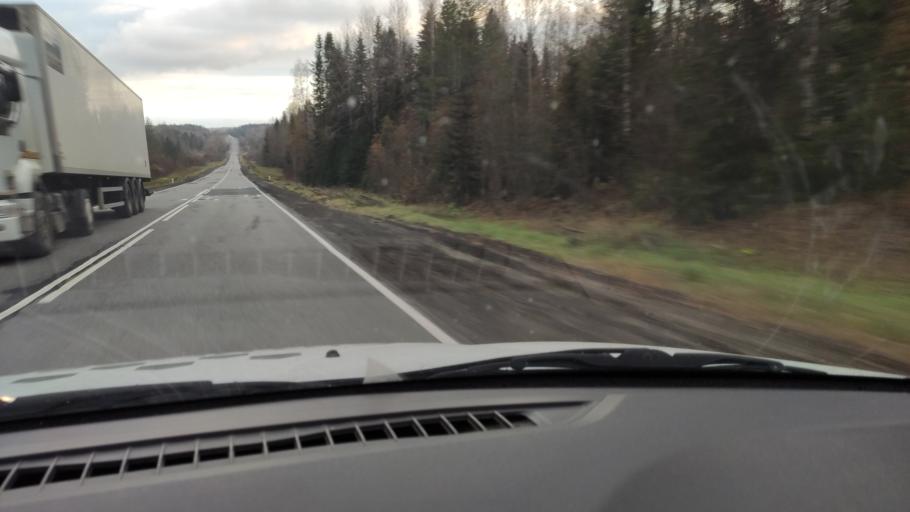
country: RU
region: Kirov
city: Omutninsk
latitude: 58.7344
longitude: 52.0734
